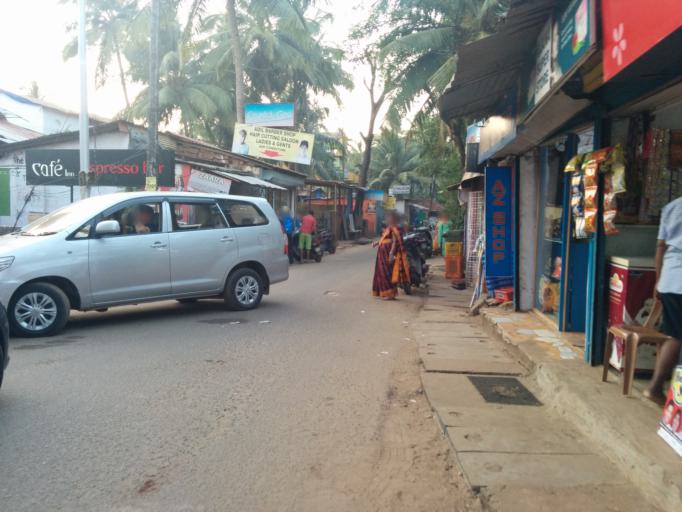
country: IN
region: Goa
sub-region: South Goa
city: Kankon
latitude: 15.0132
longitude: 74.0224
